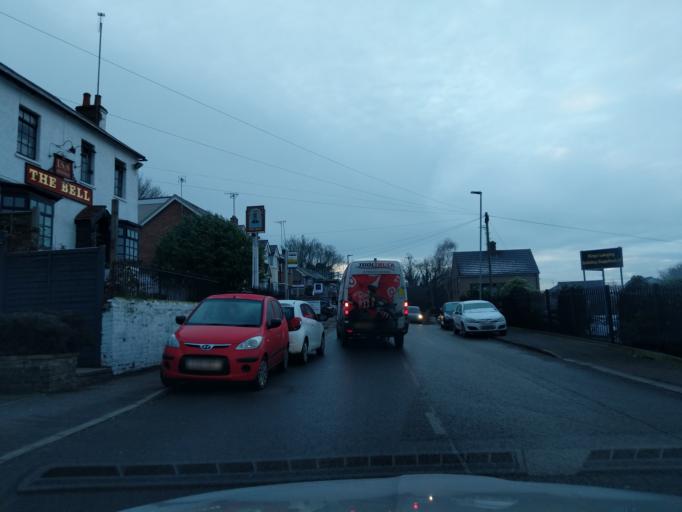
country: GB
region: England
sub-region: Hertfordshire
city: Kings Langley
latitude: 51.7152
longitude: -0.4417
